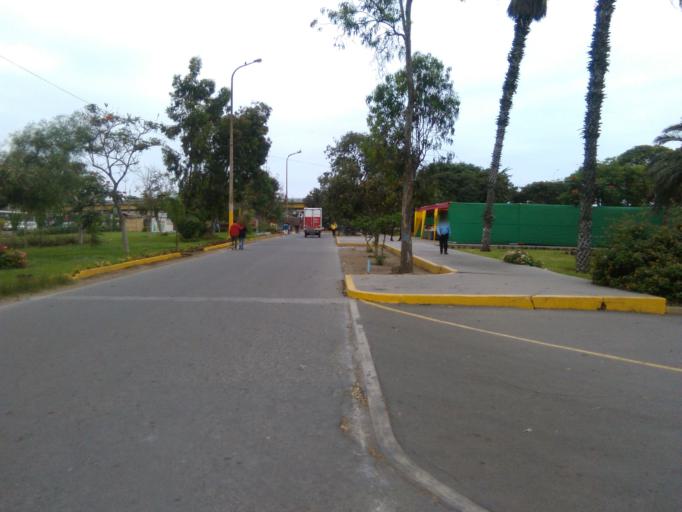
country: PE
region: Callao
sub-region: Callao
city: Callao
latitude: -12.0587
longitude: -77.0799
